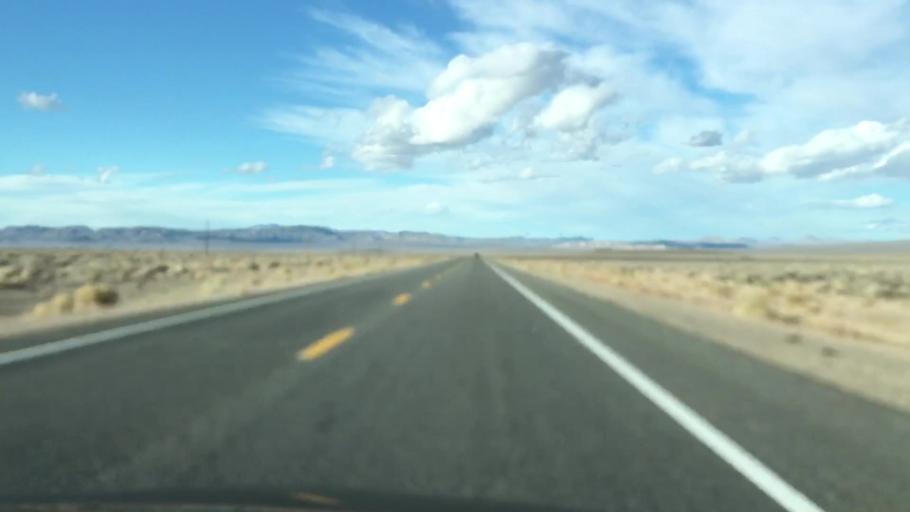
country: US
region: Nevada
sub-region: Esmeralda County
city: Goldfield
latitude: 37.3954
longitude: -117.1467
